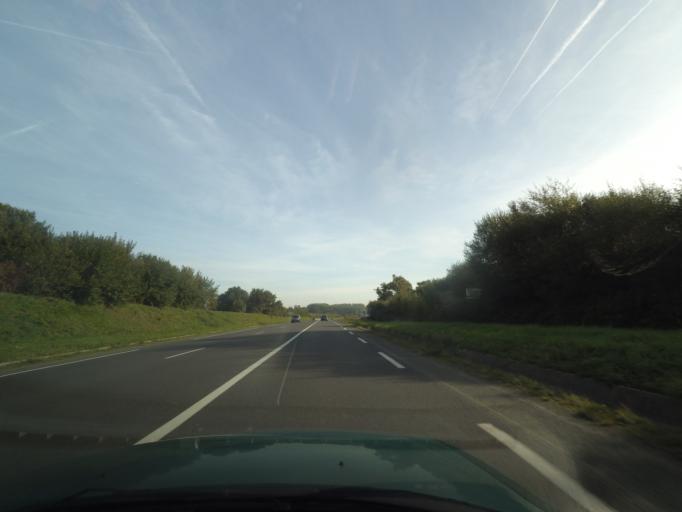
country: FR
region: Pays de la Loire
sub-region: Departement de la Vendee
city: Montaigu
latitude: 46.9615
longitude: -1.3152
